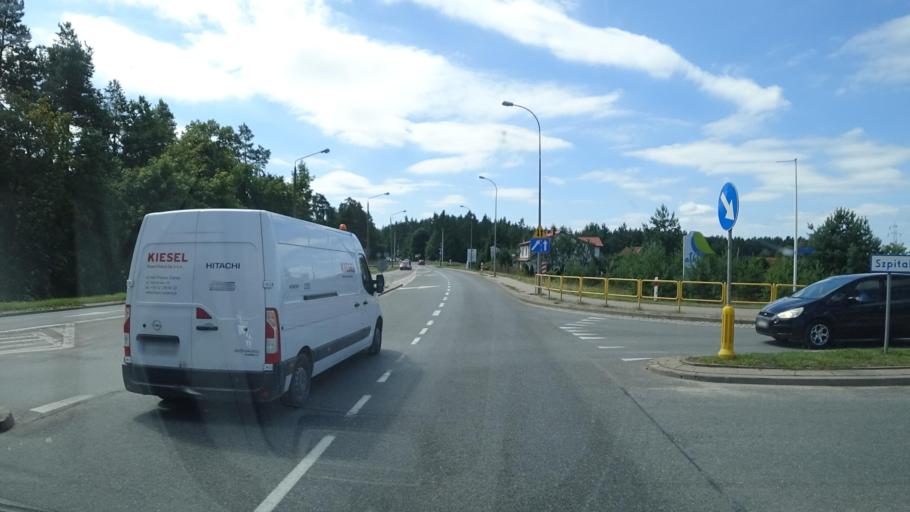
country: PL
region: Warmian-Masurian Voivodeship
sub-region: Powiat elcki
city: Elk
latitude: 53.7956
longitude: 22.3561
